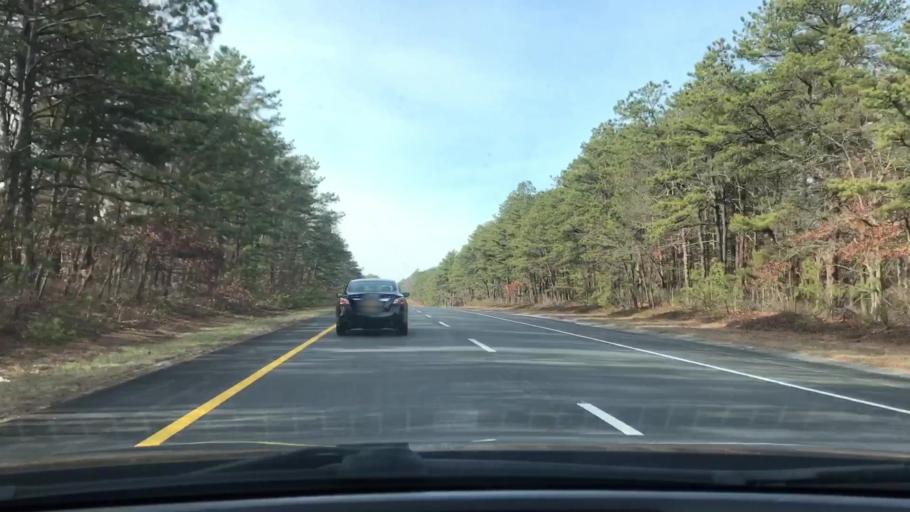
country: US
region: New York
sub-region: Suffolk County
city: Calverton
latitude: 40.9070
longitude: -72.7059
